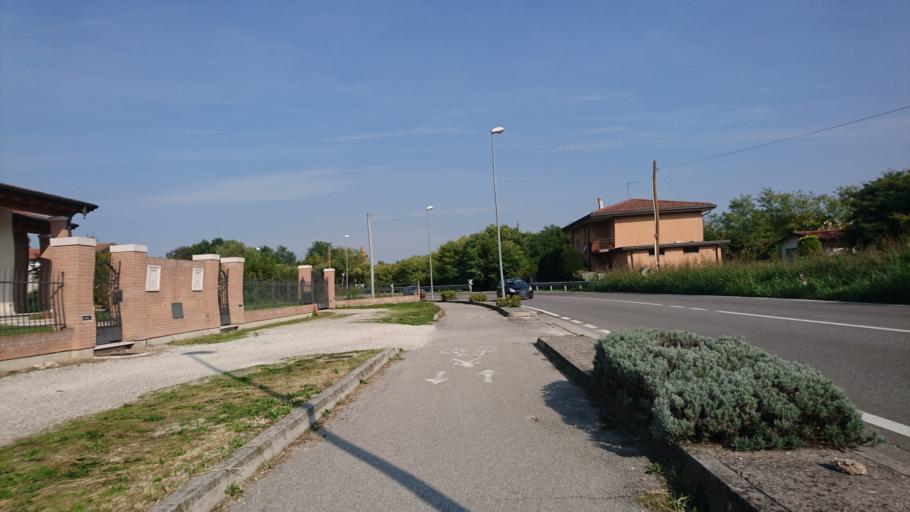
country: IT
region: Veneto
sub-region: Provincia di Padova
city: Villaguattera
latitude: 45.4442
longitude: 11.8278
